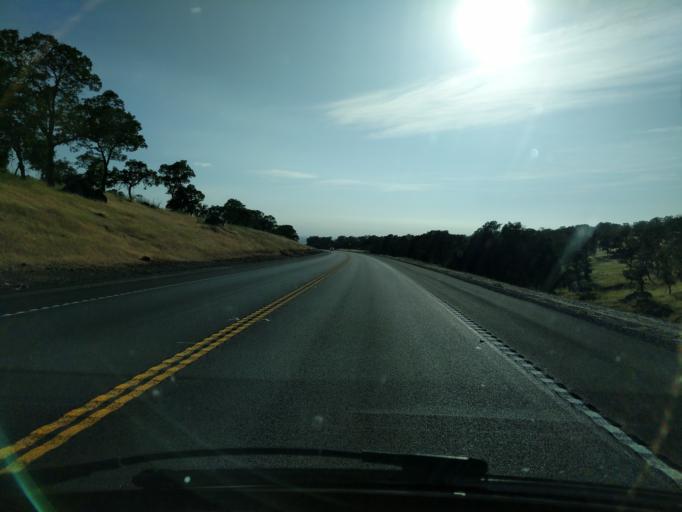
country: US
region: California
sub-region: Calaveras County
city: Copperopolis
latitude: 37.9435
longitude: -120.7299
